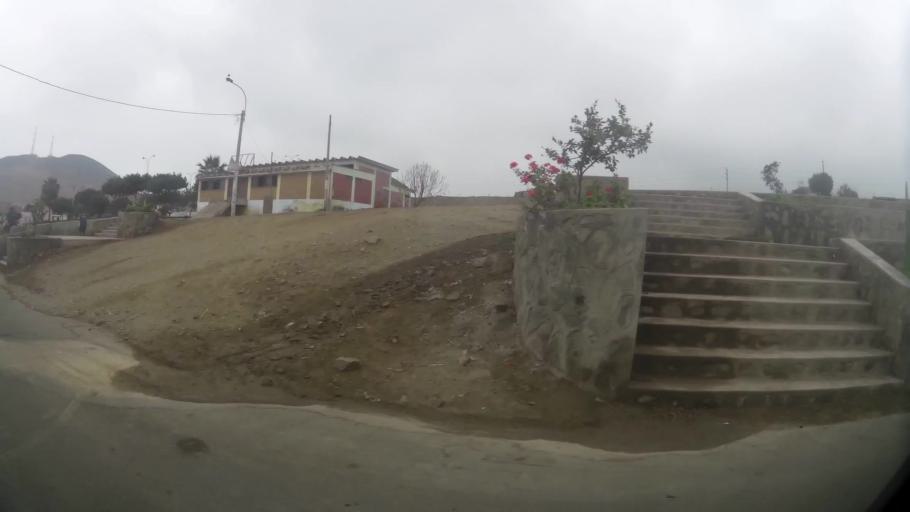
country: PE
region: Lima
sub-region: Provincia de Huaral
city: Chancay
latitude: -11.5901
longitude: -77.2592
